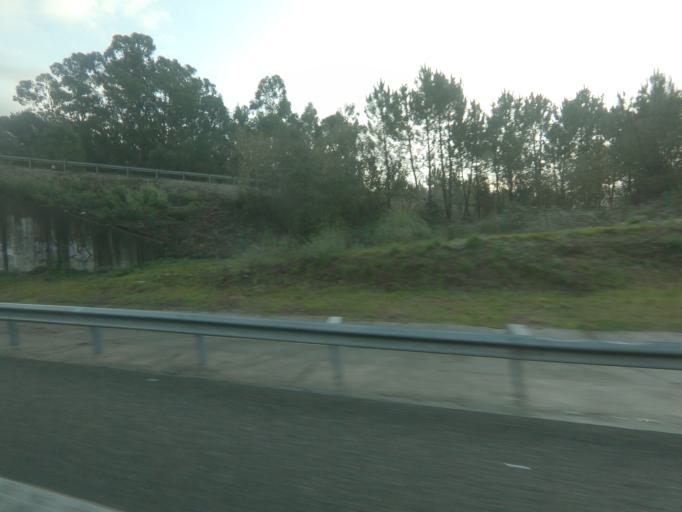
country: ES
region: Galicia
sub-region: Provincia de Pontevedra
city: Porrino
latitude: 42.1118
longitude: -8.6499
